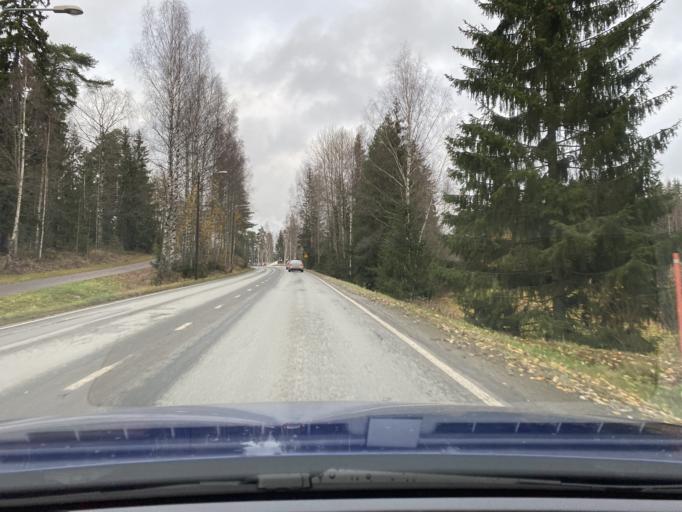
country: FI
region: Pirkanmaa
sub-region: Tampere
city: Lempaeaelae
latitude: 61.3360
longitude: 23.7513
